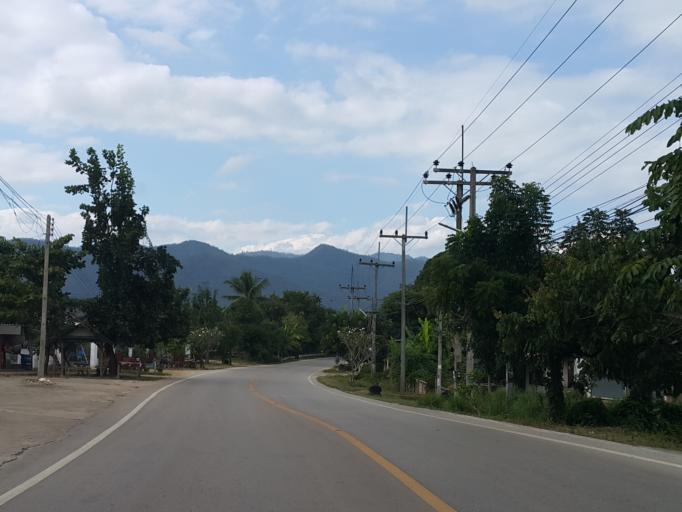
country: TH
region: Lampang
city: Chae Hom
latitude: 18.5723
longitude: 99.4702
